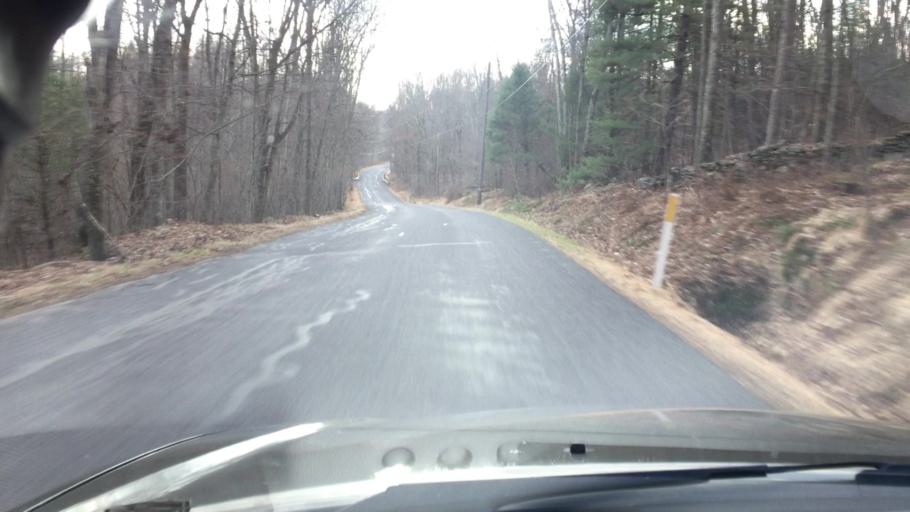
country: US
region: Pennsylvania
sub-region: Luzerne County
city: Back Mountain
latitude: 41.2963
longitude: -76.0471
